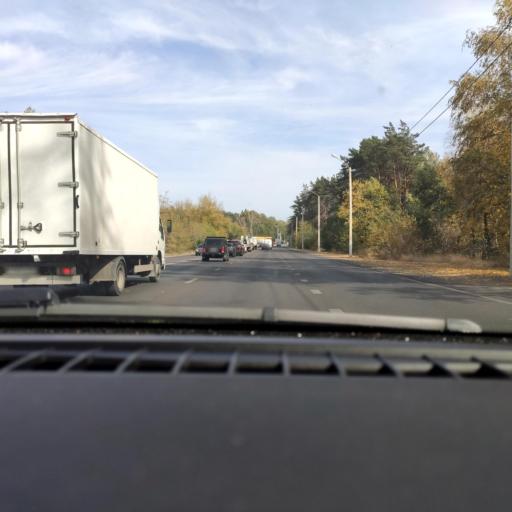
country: RU
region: Voronezj
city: Voronezh
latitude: 51.6808
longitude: 39.2751
